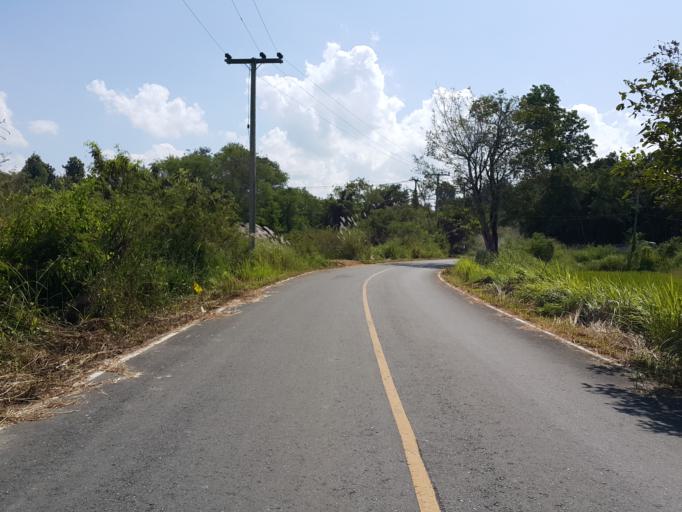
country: TH
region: Chiang Mai
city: Mae On
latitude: 18.8623
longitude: 99.1665
